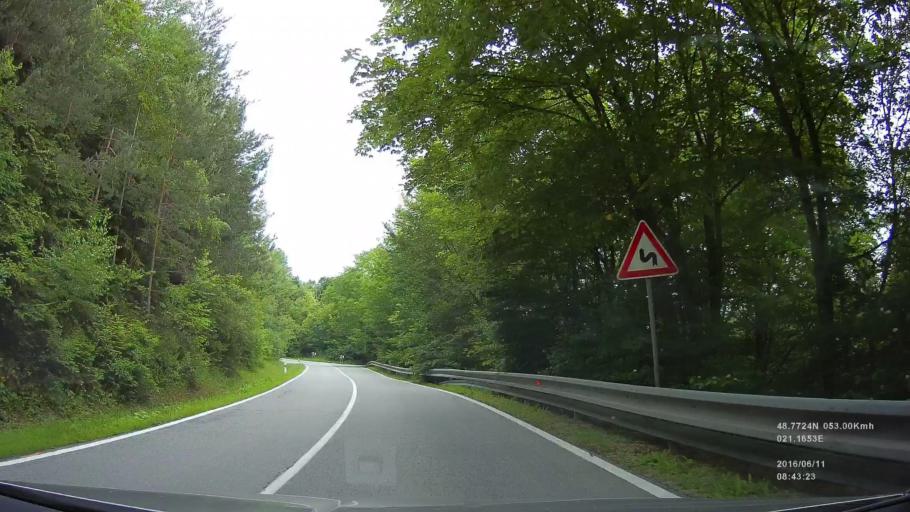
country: SK
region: Kosicky
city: Kosice
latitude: 48.7673
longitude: 21.1655
